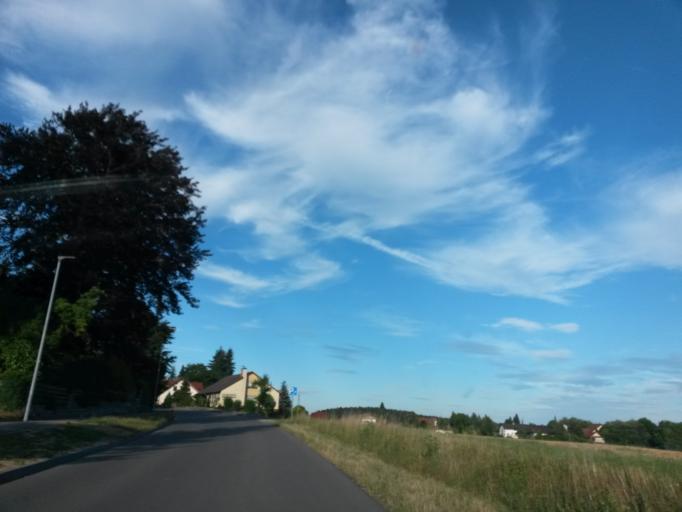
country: DE
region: Baden-Wuerttemberg
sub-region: Regierungsbezirk Stuttgart
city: Ellenberg
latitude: 49.0518
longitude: 10.2227
